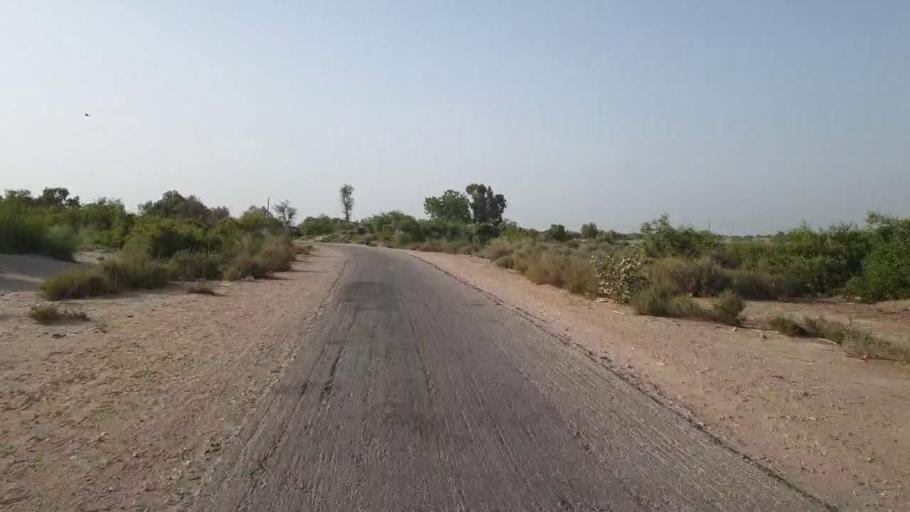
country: PK
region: Sindh
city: Jam Sahib
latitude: 26.4867
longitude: 68.8607
